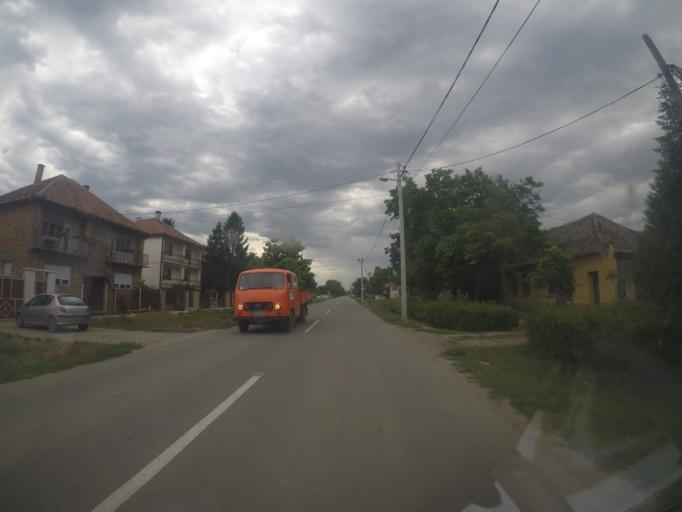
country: RS
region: Autonomna Pokrajina Vojvodina
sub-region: Juznobanatski Okrug
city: Opovo
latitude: 45.0538
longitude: 20.4261
